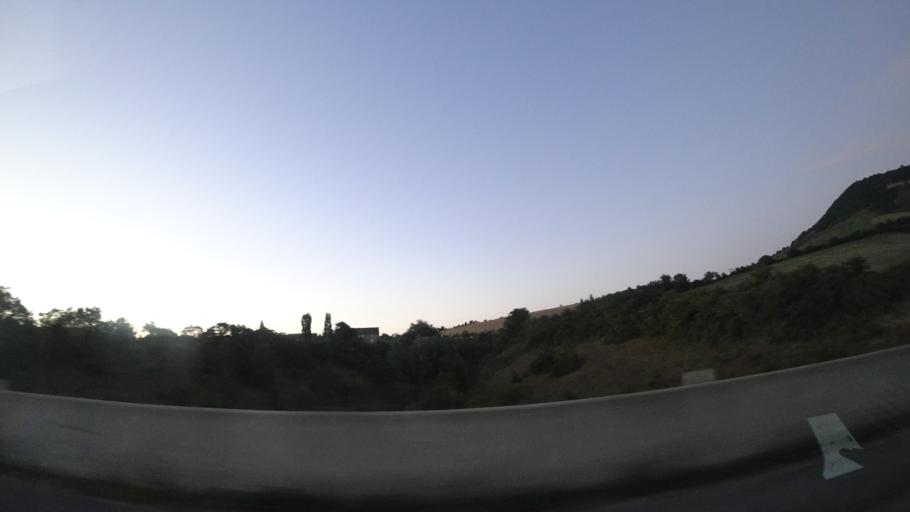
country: FR
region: Midi-Pyrenees
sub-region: Departement de l'Aveyron
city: Creissels
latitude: 44.1343
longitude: 3.0402
